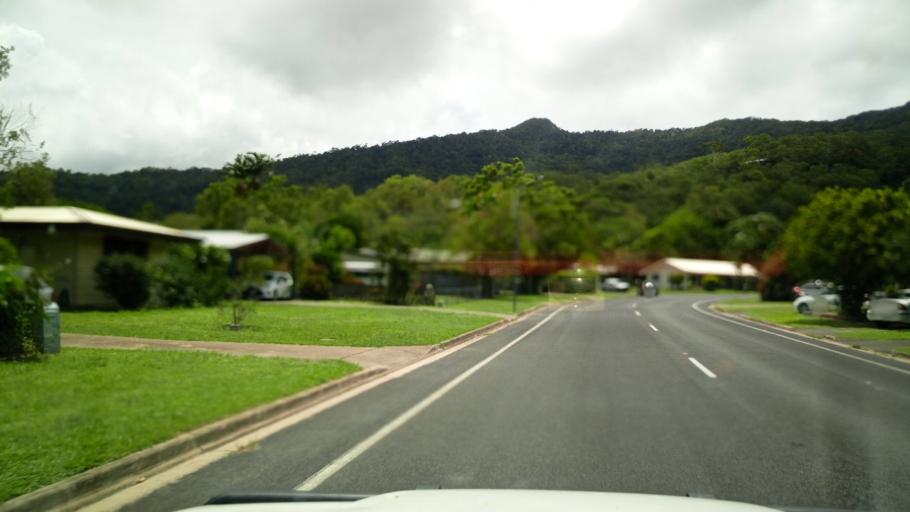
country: AU
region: Queensland
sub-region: Cairns
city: Yorkeys Knob
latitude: -16.8343
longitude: 145.6873
